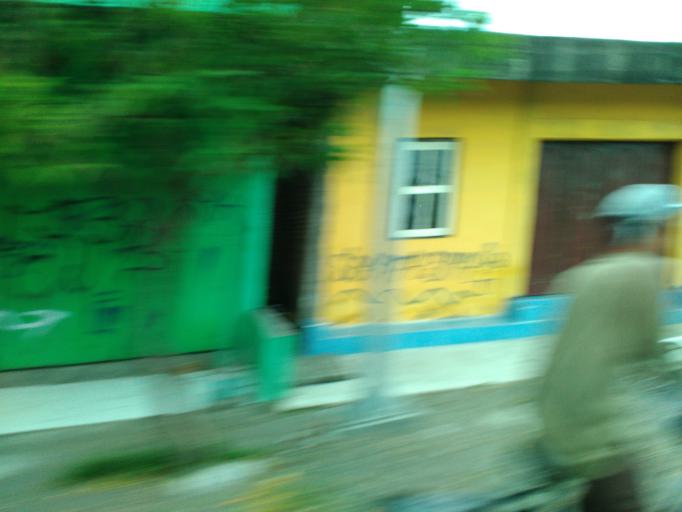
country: ID
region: Central Java
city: Gatak
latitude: -7.5822
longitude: 110.7142
